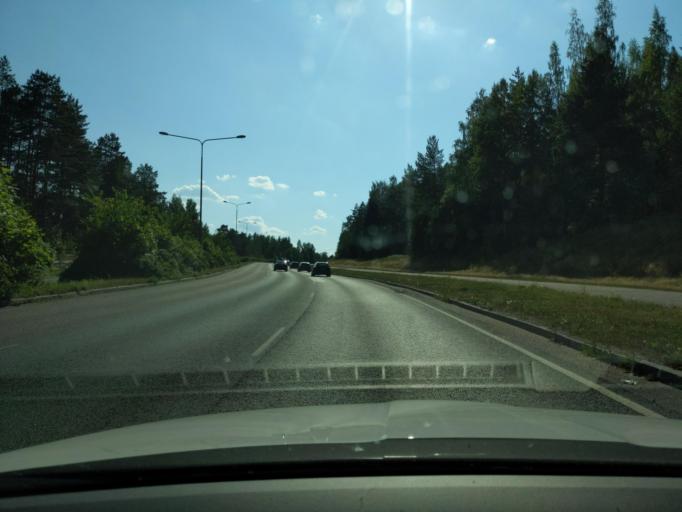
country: FI
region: Paijanne Tavastia
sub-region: Lahti
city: Lahti
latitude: 60.9810
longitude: 25.6221
